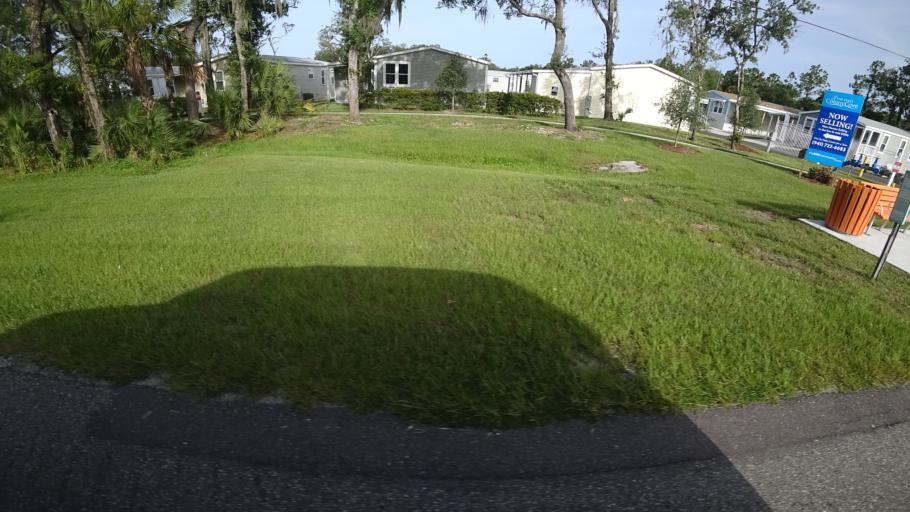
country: US
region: Florida
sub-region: Manatee County
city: Ellenton
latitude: 27.5429
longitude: -82.4911
